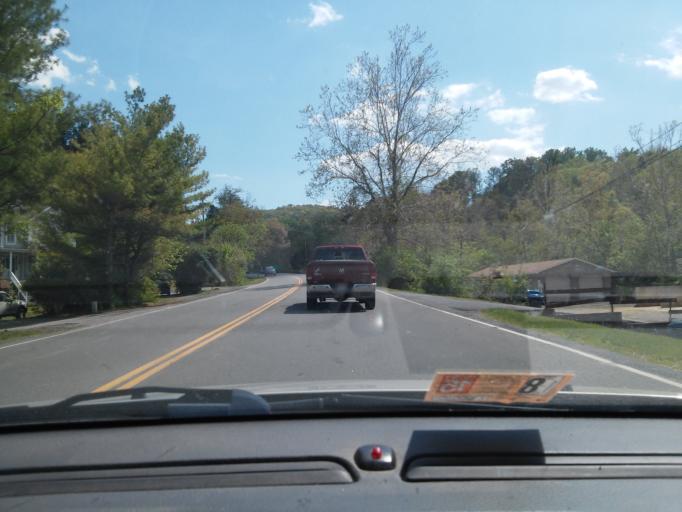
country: US
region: Virginia
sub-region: Warren County
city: Front Royal
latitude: 38.9053
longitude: -78.1850
